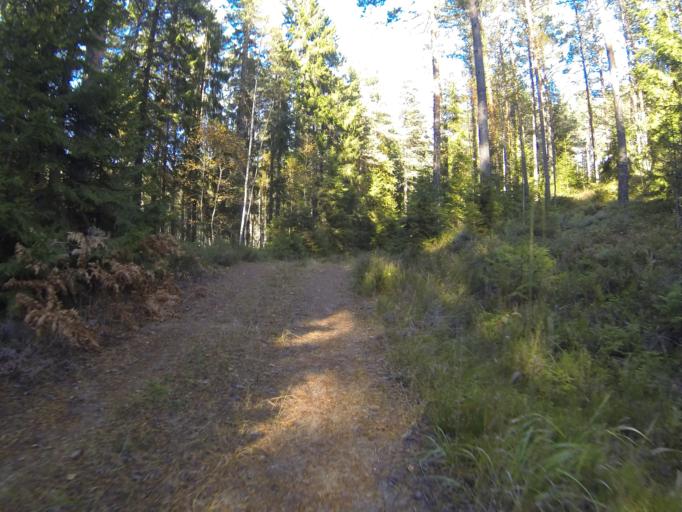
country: FI
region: Varsinais-Suomi
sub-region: Salo
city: Saerkisalo
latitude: 60.2100
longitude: 22.9632
